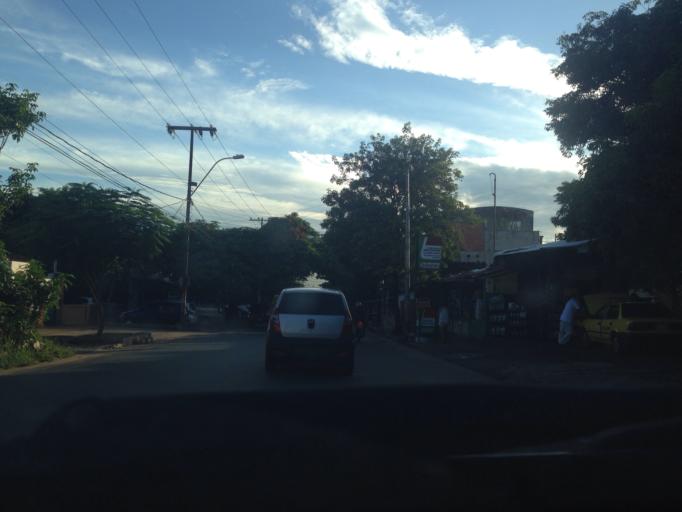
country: PY
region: Central
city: Lambare
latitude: -25.3268
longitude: -57.5833
